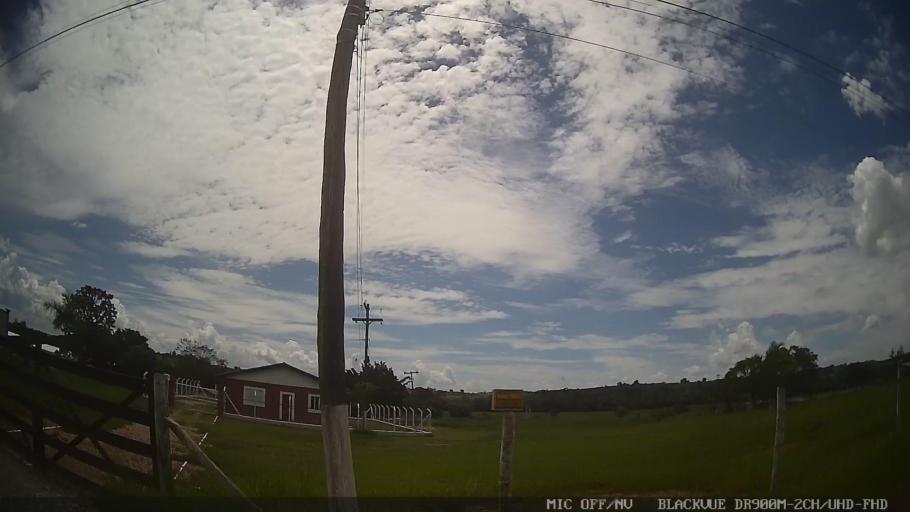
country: BR
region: Sao Paulo
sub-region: Conchas
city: Conchas
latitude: -23.0920
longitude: -47.9837
